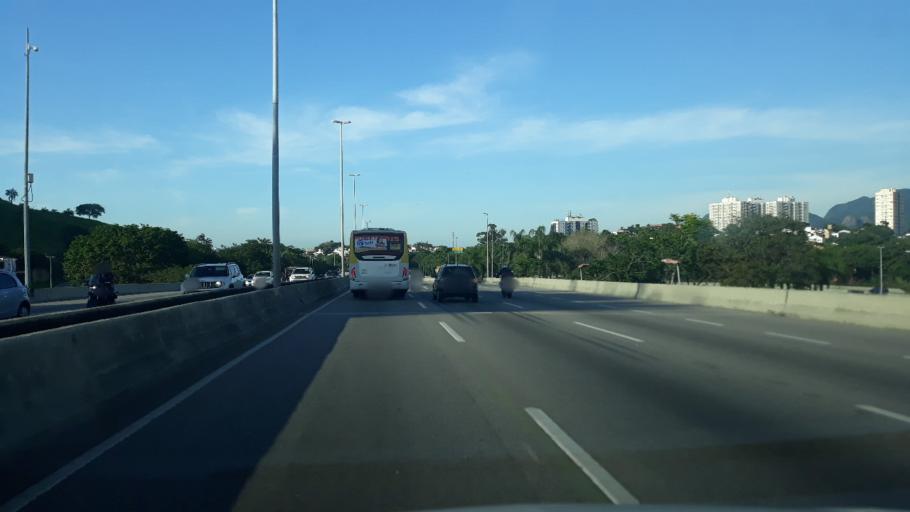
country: BR
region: Rio de Janeiro
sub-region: Sao Joao De Meriti
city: Sao Joao de Meriti
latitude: -22.9383
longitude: -43.3493
